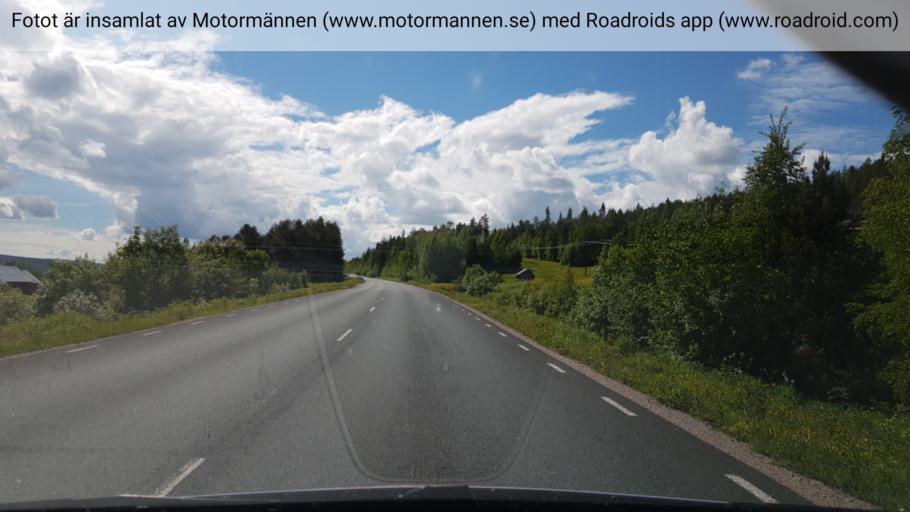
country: SE
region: Norrbotten
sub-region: Overtornea Kommun
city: OEvertornea
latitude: 66.3577
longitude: 23.6479
